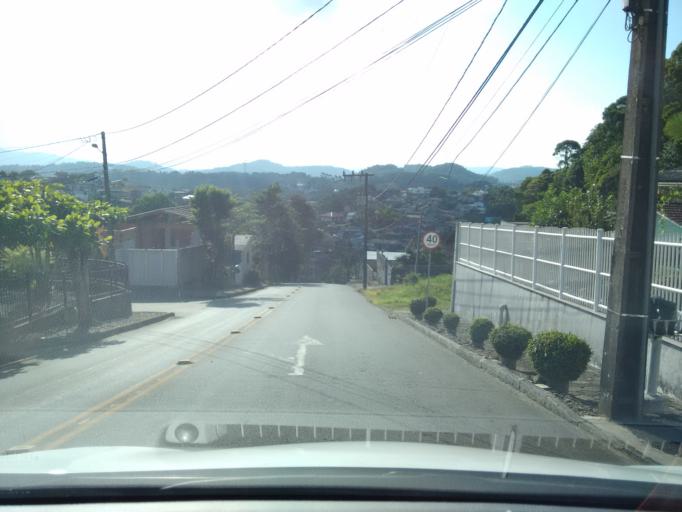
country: BR
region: Santa Catarina
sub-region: Blumenau
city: Blumenau
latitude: -26.8697
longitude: -49.0773
